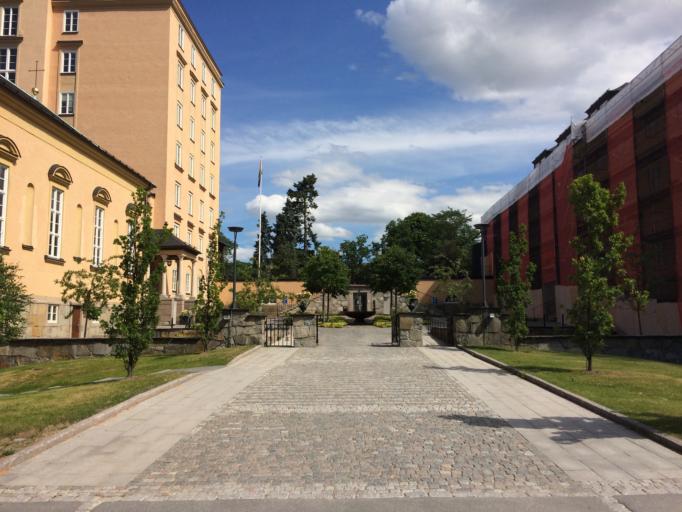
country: SE
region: Stockholm
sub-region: Stockholms Kommun
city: Stockholm
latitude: 59.3496
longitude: 18.0700
